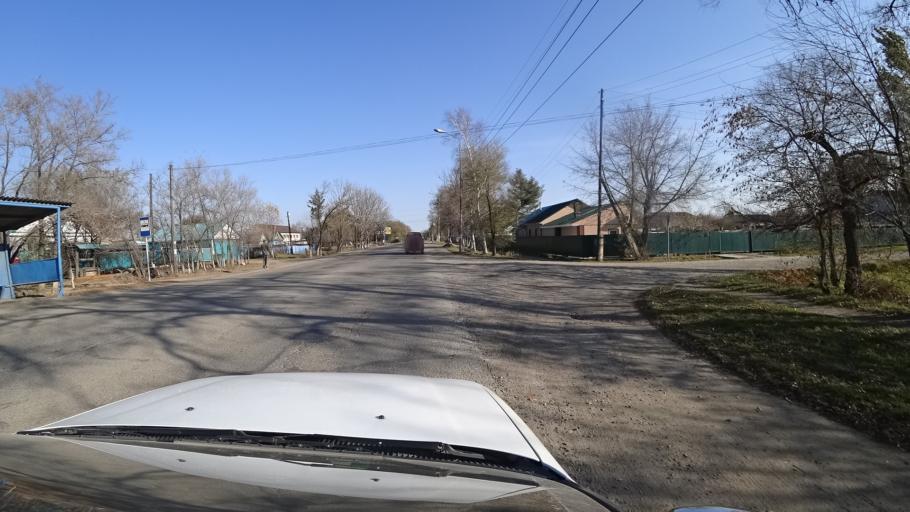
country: RU
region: Primorskiy
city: Dal'nerechensk
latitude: 45.9222
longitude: 133.7491
